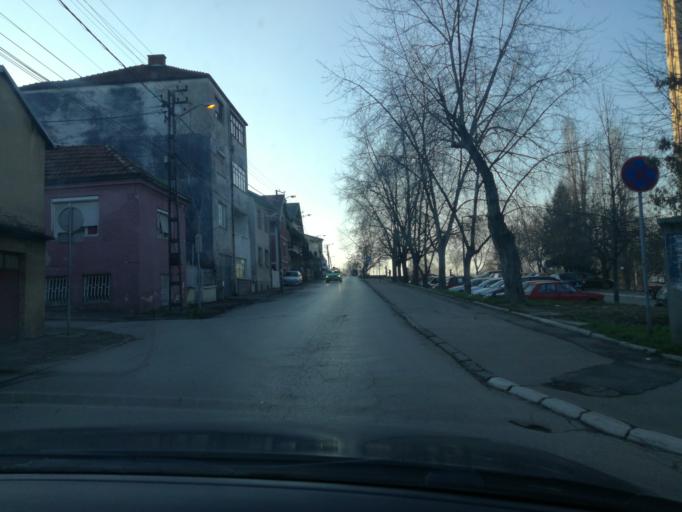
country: RS
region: Central Serbia
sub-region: Nisavski Okrug
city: Nis
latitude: 43.3110
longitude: 21.8848
